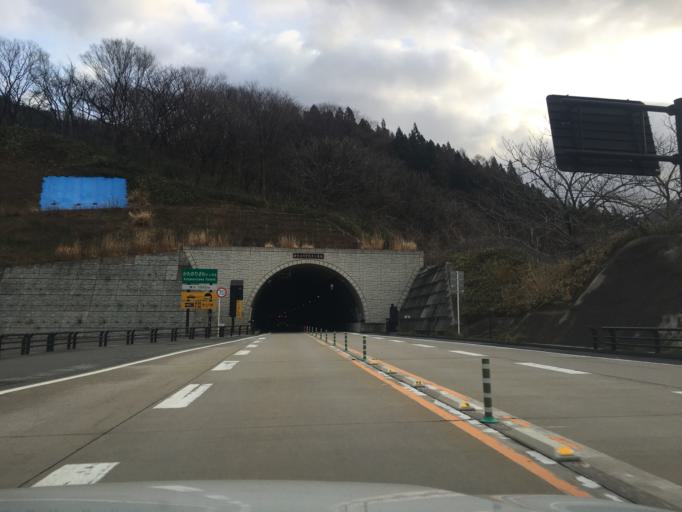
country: JP
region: Yamagata
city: Tsuruoka
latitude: 38.6676
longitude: 139.6252
